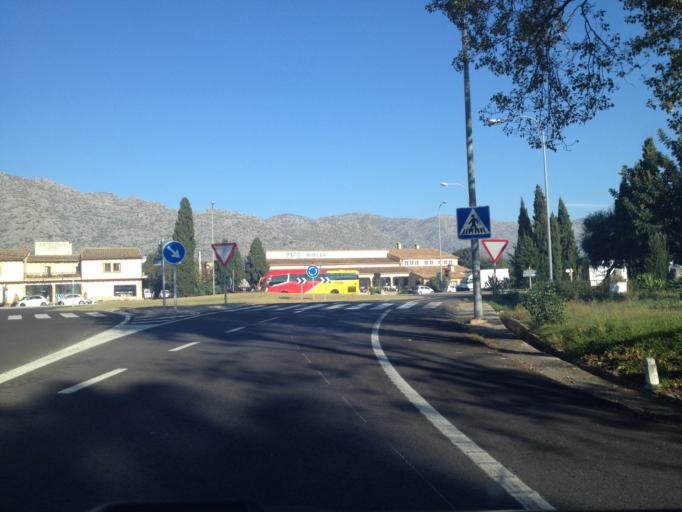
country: ES
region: Balearic Islands
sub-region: Illes Balears
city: Pollenca
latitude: 39.8839
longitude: 3.0225
